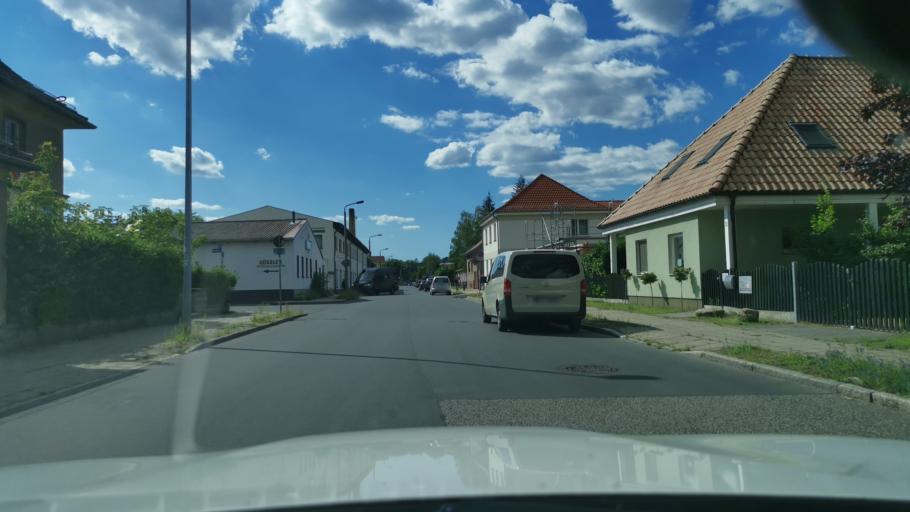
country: DE
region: Brandenburg
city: Luckenwalde
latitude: 52.0965
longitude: 13.1627
